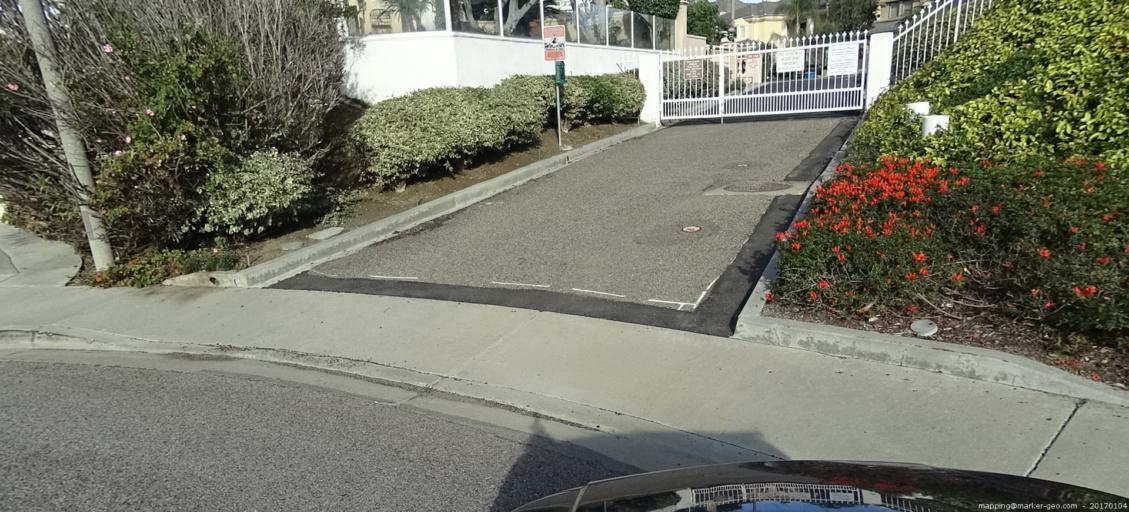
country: US
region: California
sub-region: Orange County
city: Laguna Niguel
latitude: 33.4973
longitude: -117.7278
